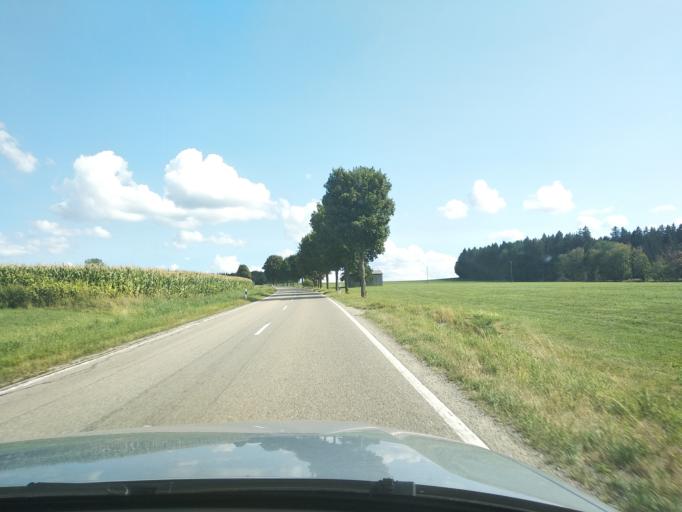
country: DE
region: Baden-Wuerttemberg
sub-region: Tuebingen Region
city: Leutkirch im Allgau
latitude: 47.8864
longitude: 9.9794
